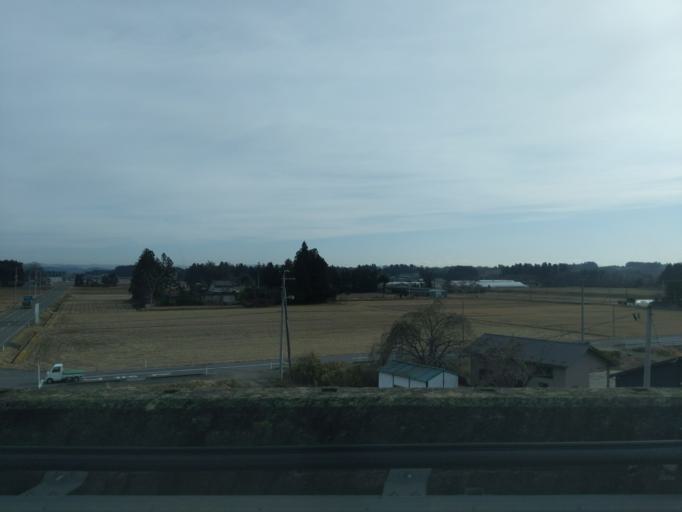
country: JP
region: Iwate
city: Ichinoseki
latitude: 38.7553
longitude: 141.0754
